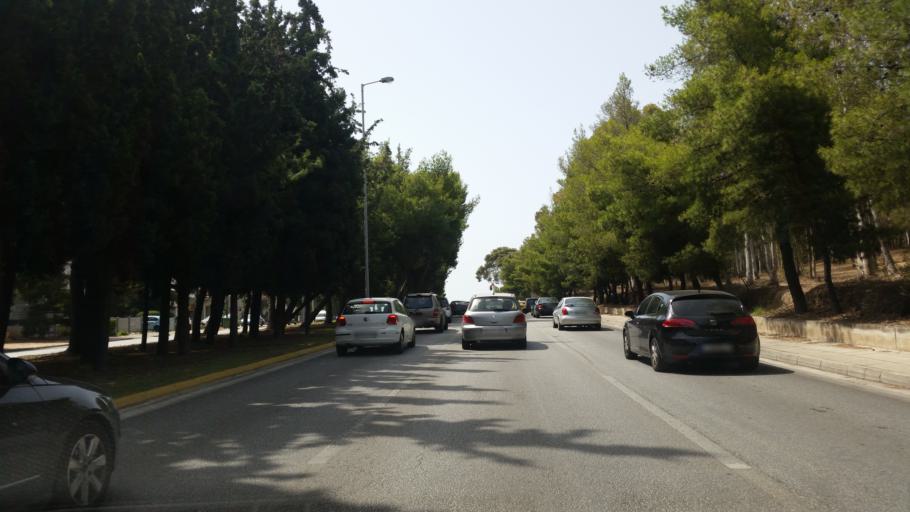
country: GR
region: Attica
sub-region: Nomarchia Anatolikis Attikis
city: Vouliagmeni
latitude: 37.8234
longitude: 23.7749
